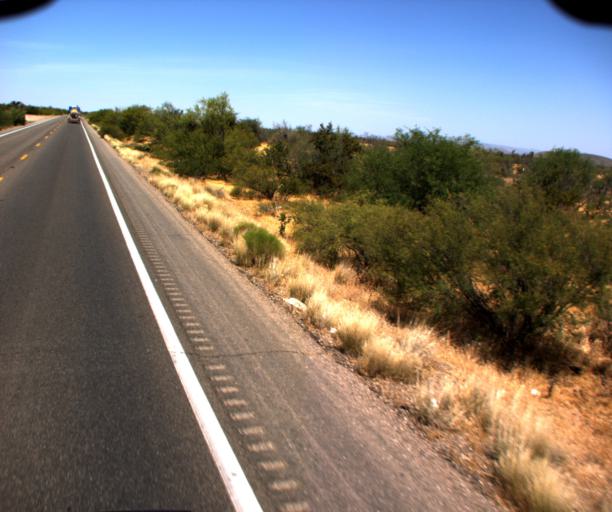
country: US
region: Arizona
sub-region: Gila County
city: Peridot
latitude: 33.3092
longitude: -110.5001
